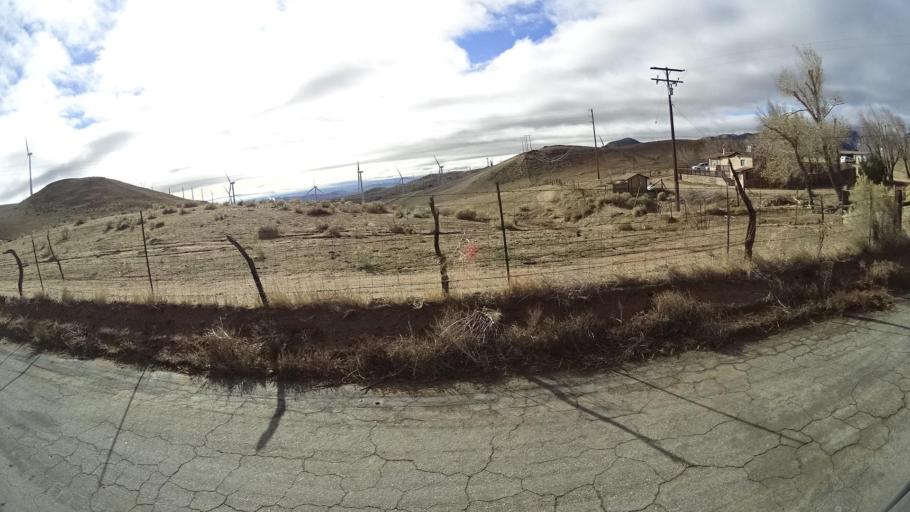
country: US
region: California
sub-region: Kern County
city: Tehachapi
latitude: 35.0703
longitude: -118.3456
